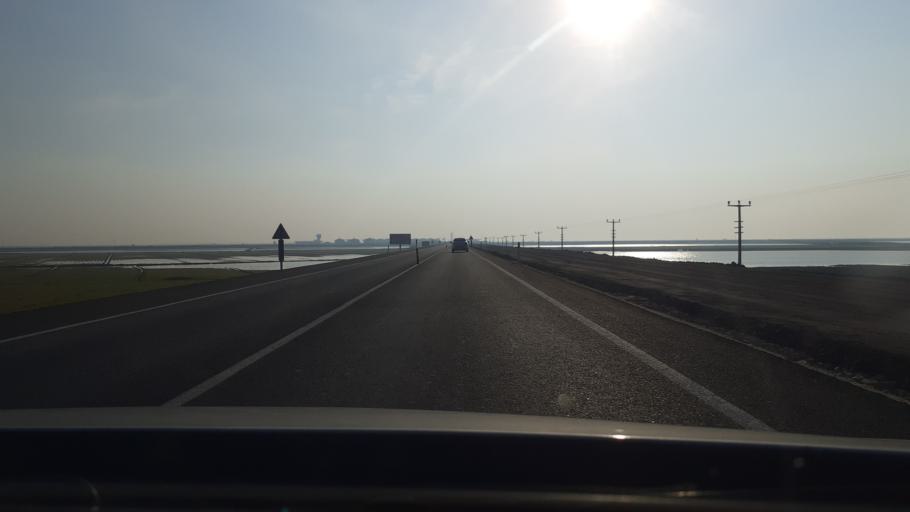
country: TR
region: Hatay
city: Serinyol
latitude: 36.3690
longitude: 36.2583
